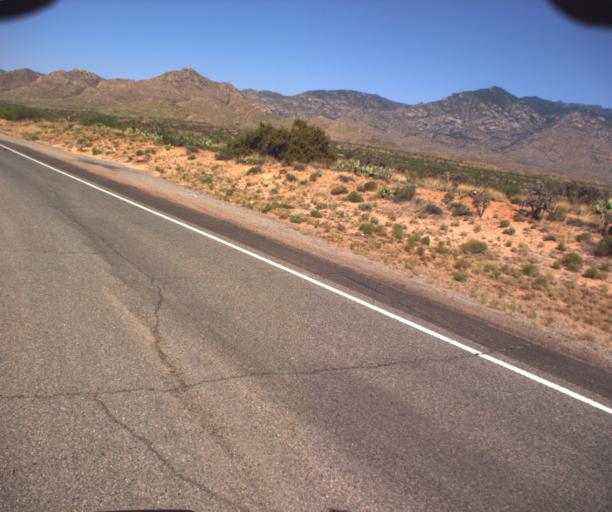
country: US
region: Arizona
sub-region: Graham County
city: Swift Trail Junction
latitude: 32.5975
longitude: -109.6860
